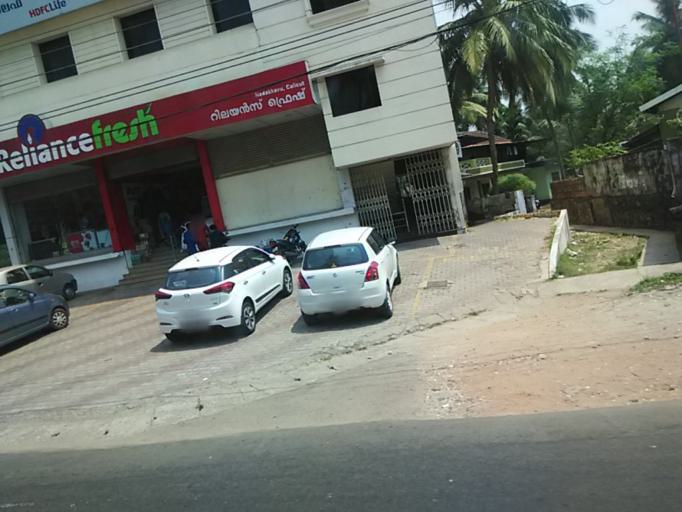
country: IN
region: Kerala
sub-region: Kozhikode
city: Kozhikode
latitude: 11.2762
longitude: 75.7722
